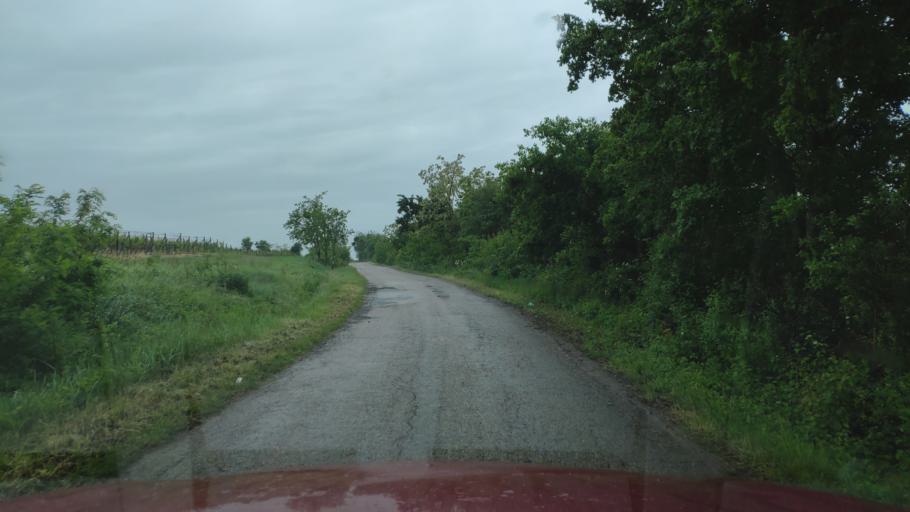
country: HU
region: Borsod-Abauj-Zemplen
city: Satoraljaujhely
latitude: 48.4257
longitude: 21.6973
